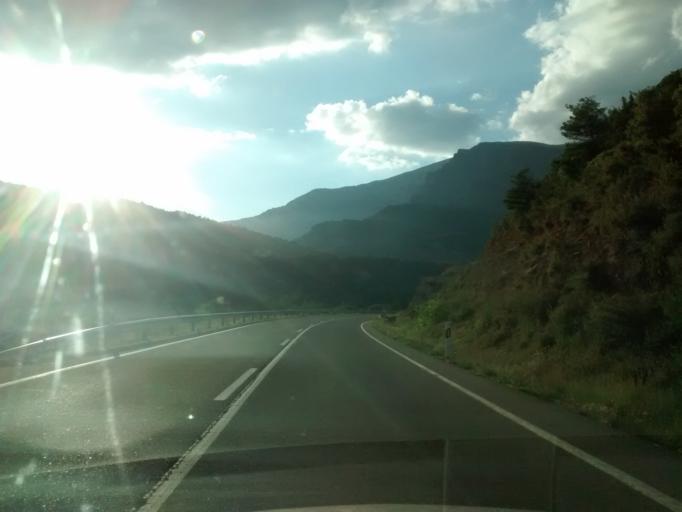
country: ES
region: Aragon
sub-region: Provincia de Huesca
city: Boltana
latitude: 42.4565
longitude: 0.0528
